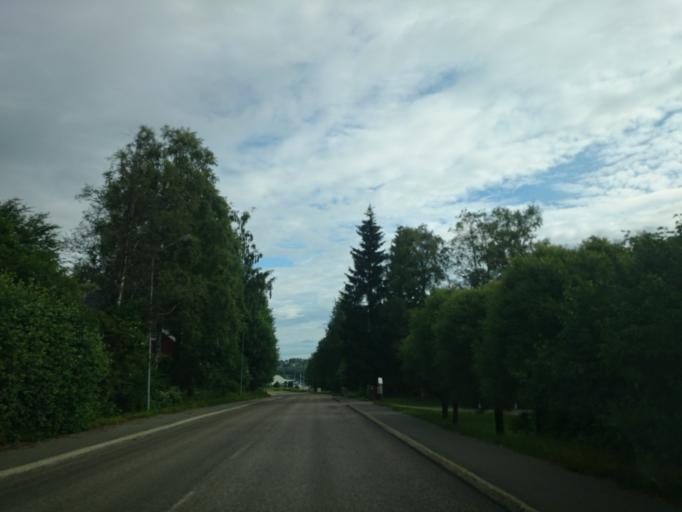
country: SE
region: Vaesternorrland
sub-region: Sundsvalls Kommun
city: Johannedal
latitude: 62.4352
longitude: 17.3869
